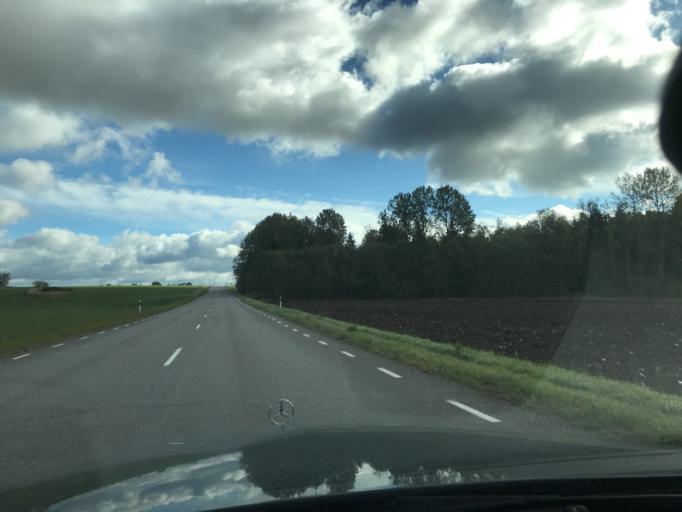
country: EE
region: Vorumaa
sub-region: Antsla vald
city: Vana-Antsla
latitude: 57.9040
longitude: 26.4617
